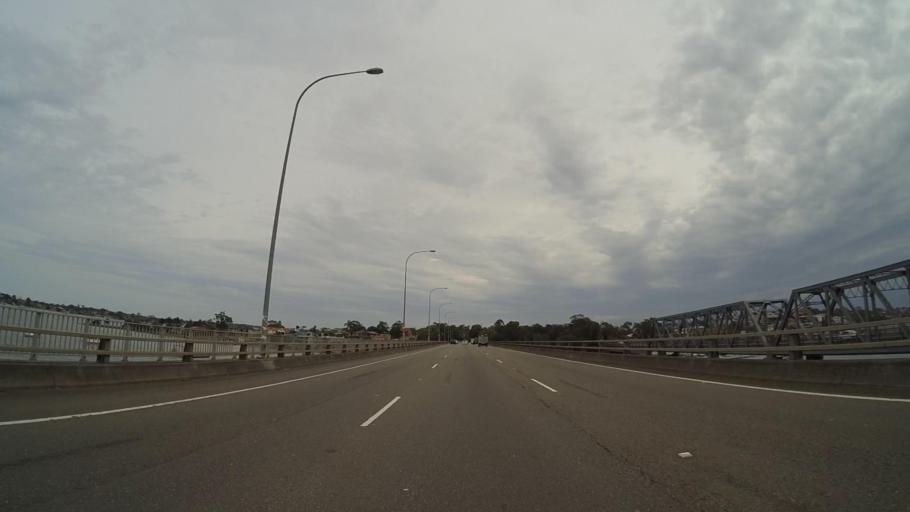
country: AU
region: New South Wales
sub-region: Kogarah
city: Blakehurst
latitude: -34.0039
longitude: 151.1134
